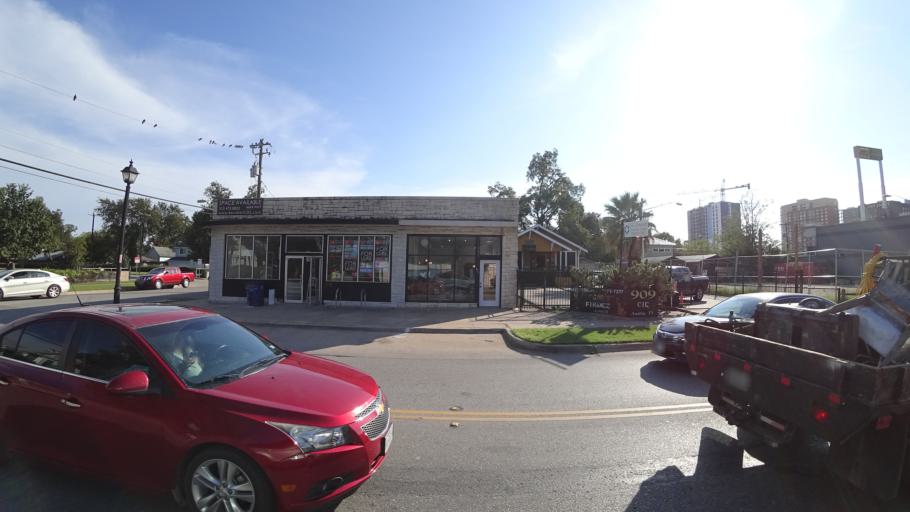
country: US
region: Texas
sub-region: Travis County
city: Austin
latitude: 30.2607
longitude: -97.7348
